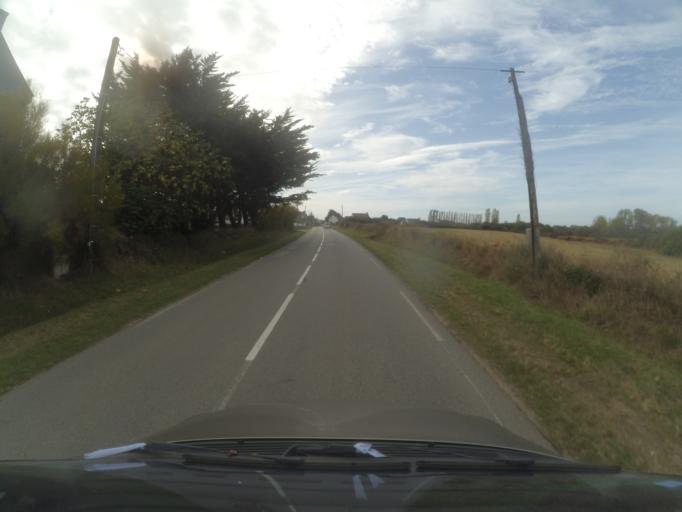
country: FR
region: Brittany
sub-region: Departement du Morbihan
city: Erdeven
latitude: 47.6254
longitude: -3.1605
